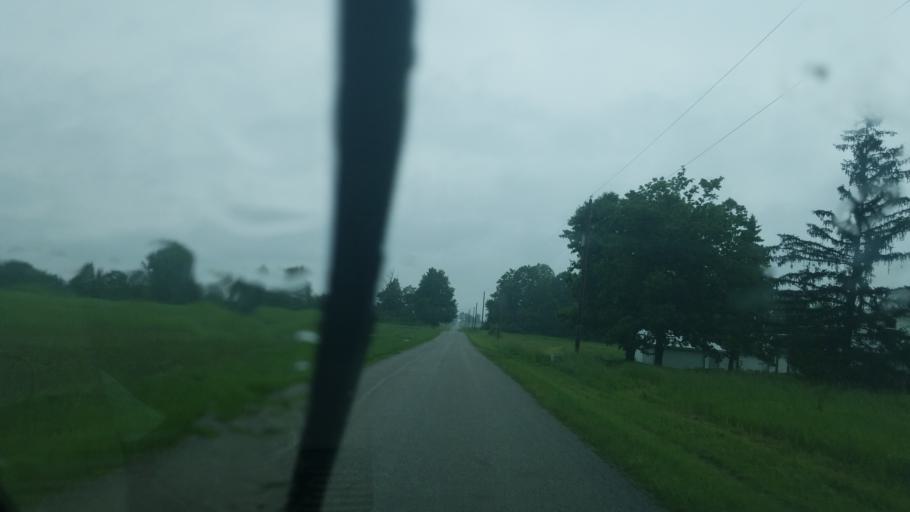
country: US
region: Ohio
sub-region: Huron County
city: Willard
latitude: 40.9298
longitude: -82.7975
